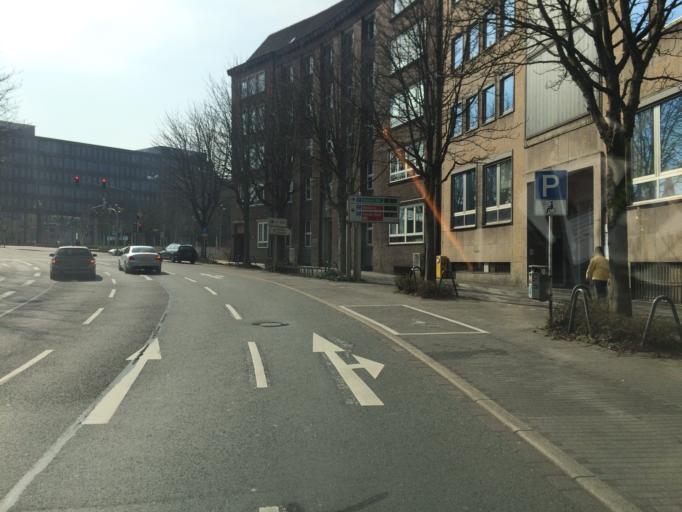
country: DE
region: North Rhine-Westphalia
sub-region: Regierungsbezirk Arnsberg
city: Dortmund
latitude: 51.5158
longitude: 7.4555
